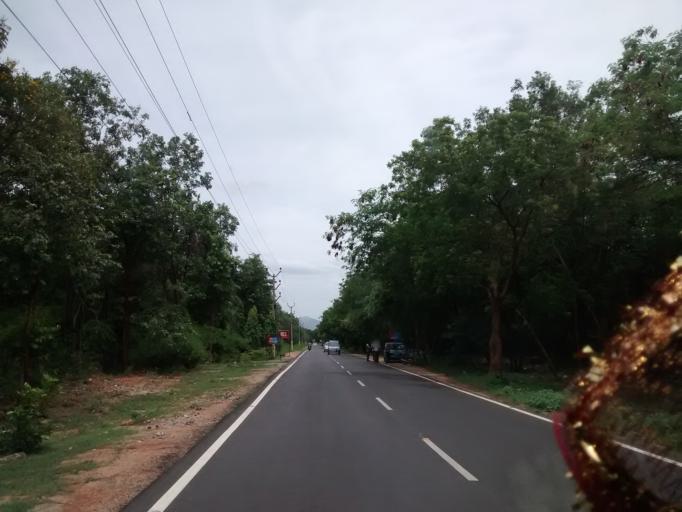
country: IN
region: Andhra Pradesh
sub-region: Chittoor
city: Tirupati
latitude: 13.6346
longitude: 79.3900
